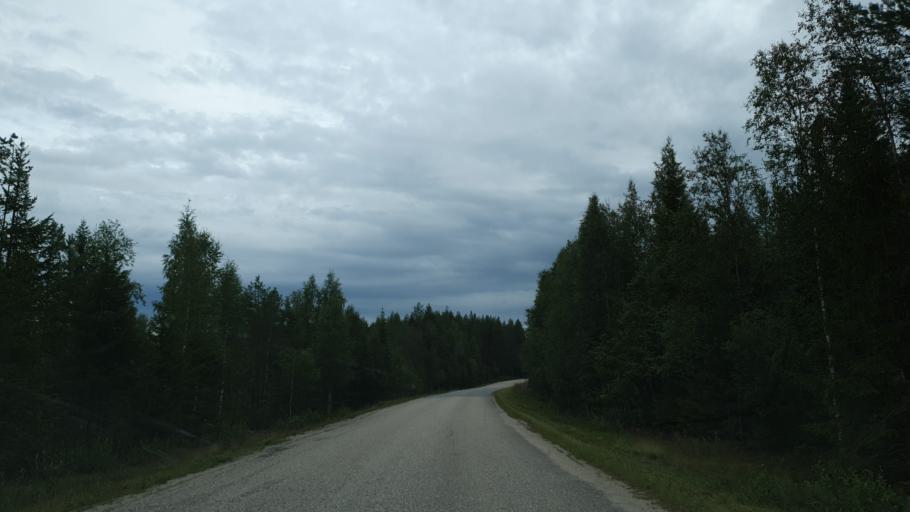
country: FI
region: Kainuu
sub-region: Kehys-Kainuu
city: Kuhmo
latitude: 64.3573
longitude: 29.1938
